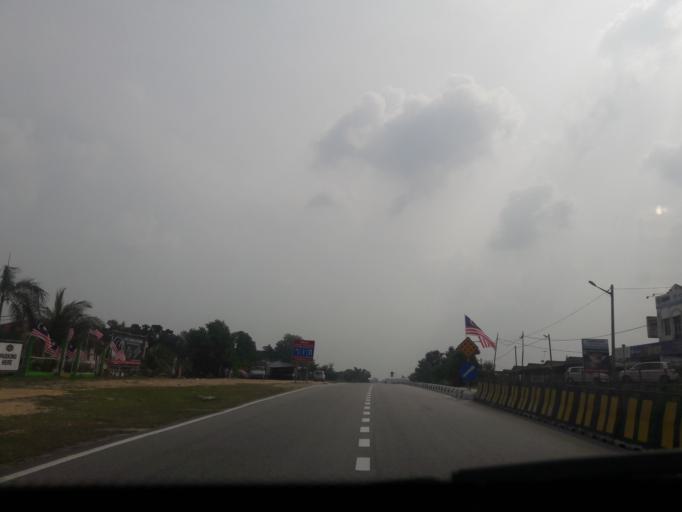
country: MY
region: Kedah
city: Kulim
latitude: 5.3708
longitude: 100.5335
